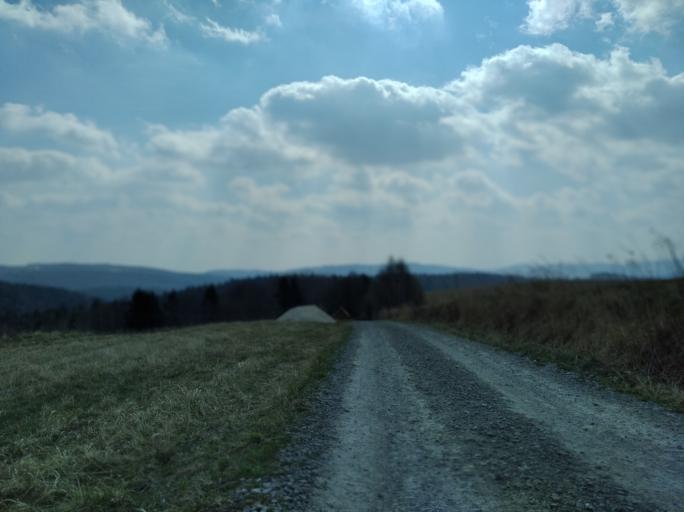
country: PL
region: Subcarpathian Voivodeship
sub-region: Powiat strzyzowski
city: Jawornik
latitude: 49.8411
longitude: 21.8544
